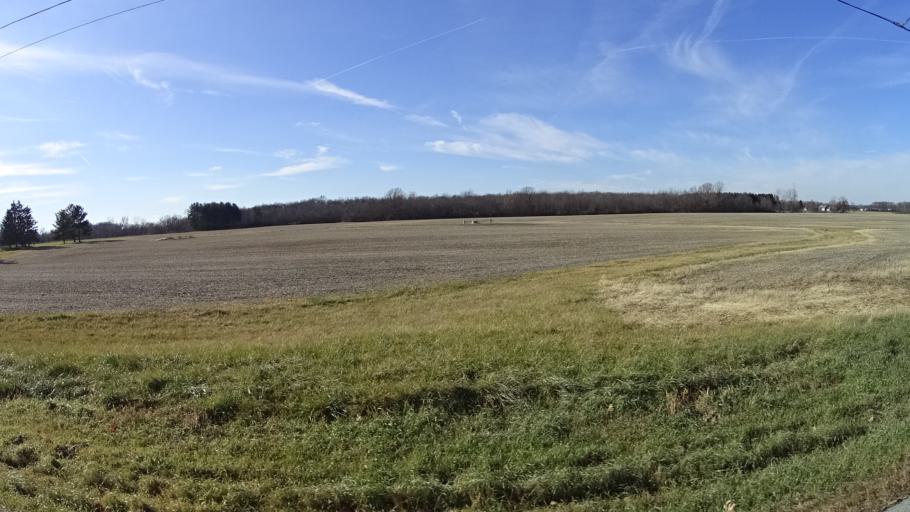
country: US
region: Ohio
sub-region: Lorain County
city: Wellington
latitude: 41.1095
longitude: -82.2200
